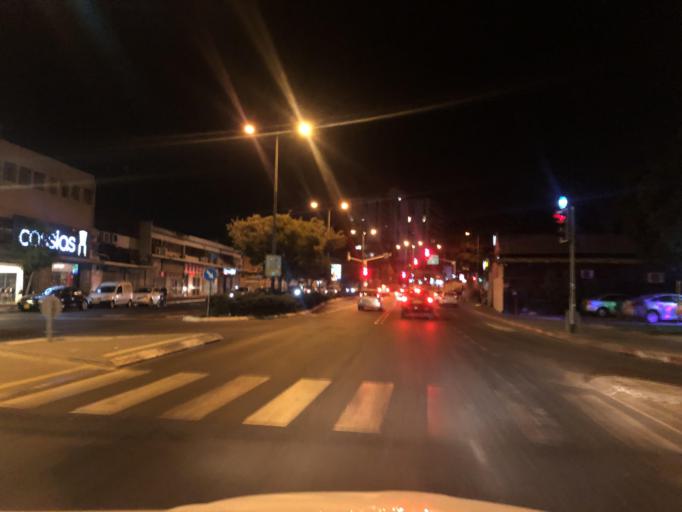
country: IL
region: Tel Aviv
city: Yafo
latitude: 32.0517
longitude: 34.7688
